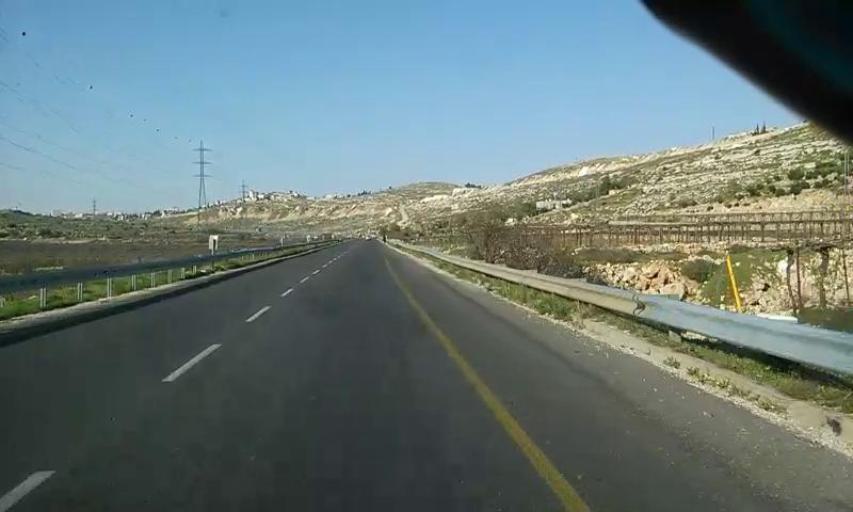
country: PS
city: Al Buq`ah
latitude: 31.5505
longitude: 35.1347
